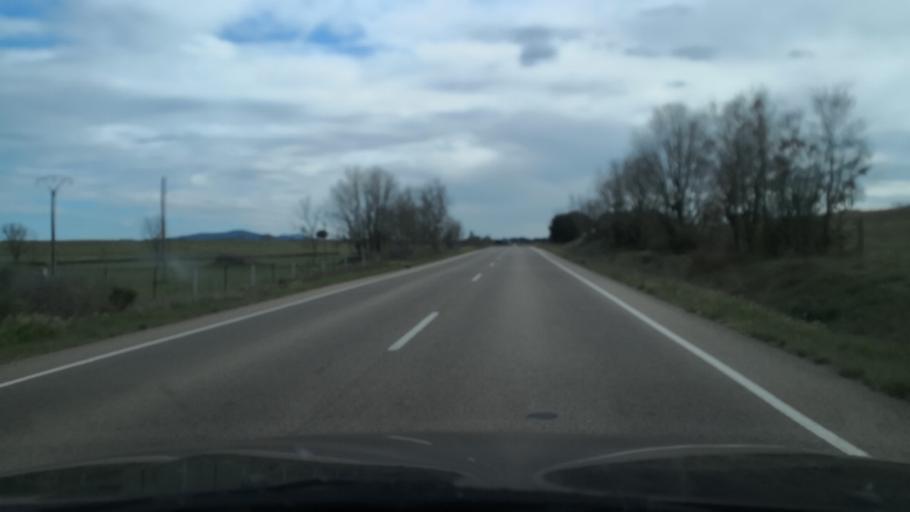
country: ES
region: Castille and Leon
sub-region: Provincia de Salamanca
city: Robleda
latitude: 40.4037
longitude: -6.6048
